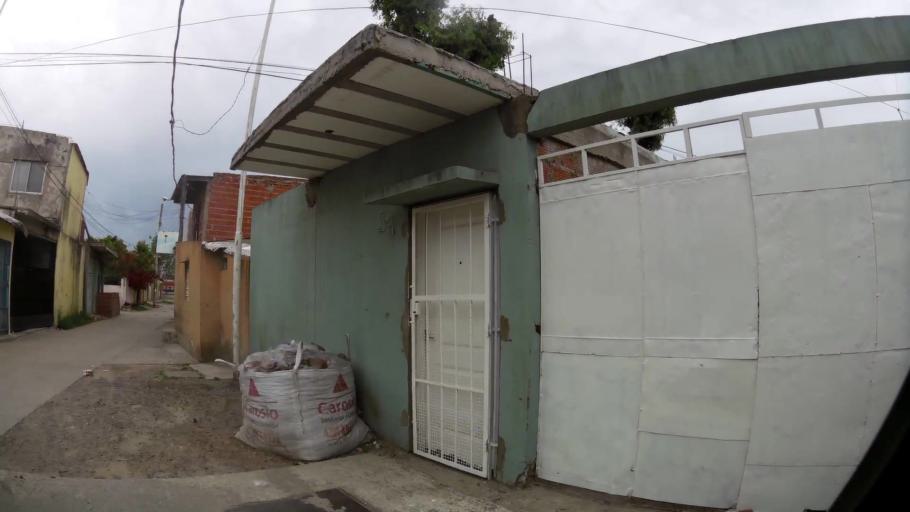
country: AR
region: Buenos Aires
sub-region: Partido de Avellaneda
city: Avellaneda
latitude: -34.6534
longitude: -58.3610
